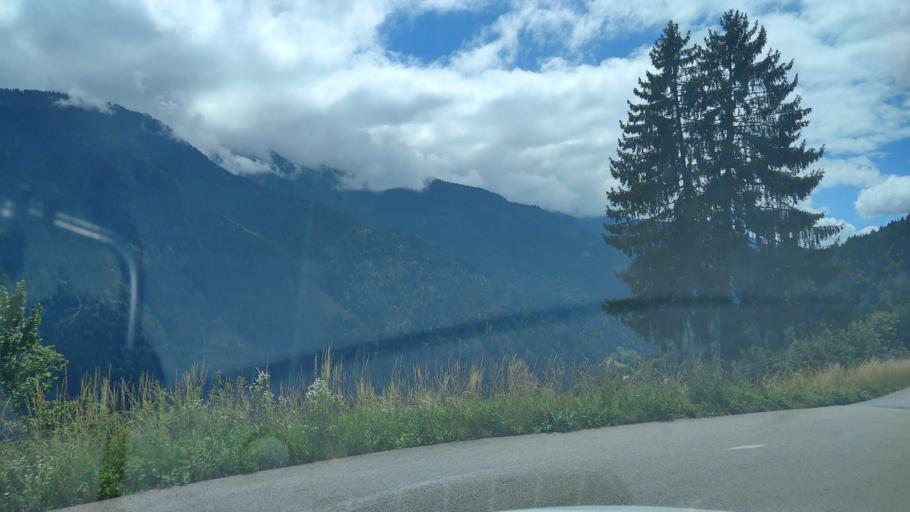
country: FR
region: Rhone-Alpes
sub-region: Departement de la Savoie
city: Beaufort
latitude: 45.7309
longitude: 6.5218
